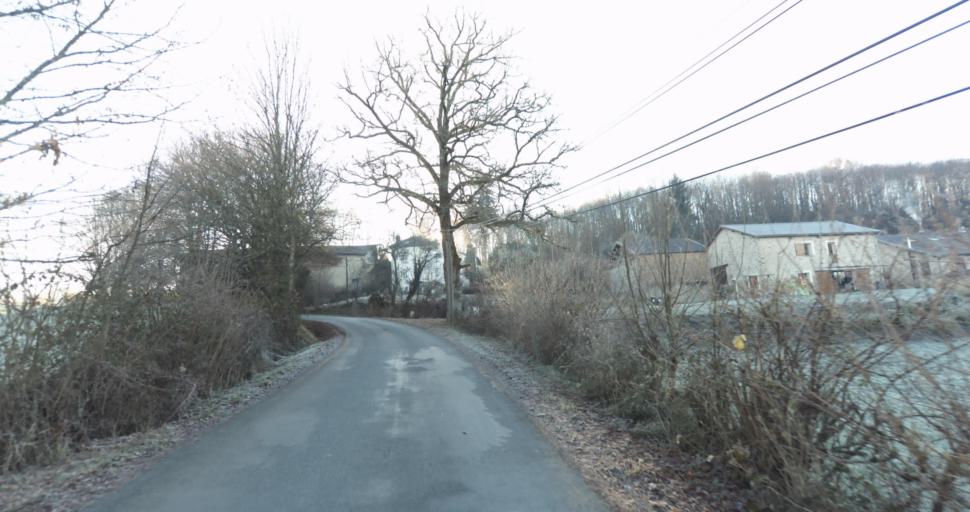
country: FR
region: Limousin
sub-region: Departement de la Haute-Vienne
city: Aixe-sur-Vienne
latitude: 45.8082
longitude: 1.1407
